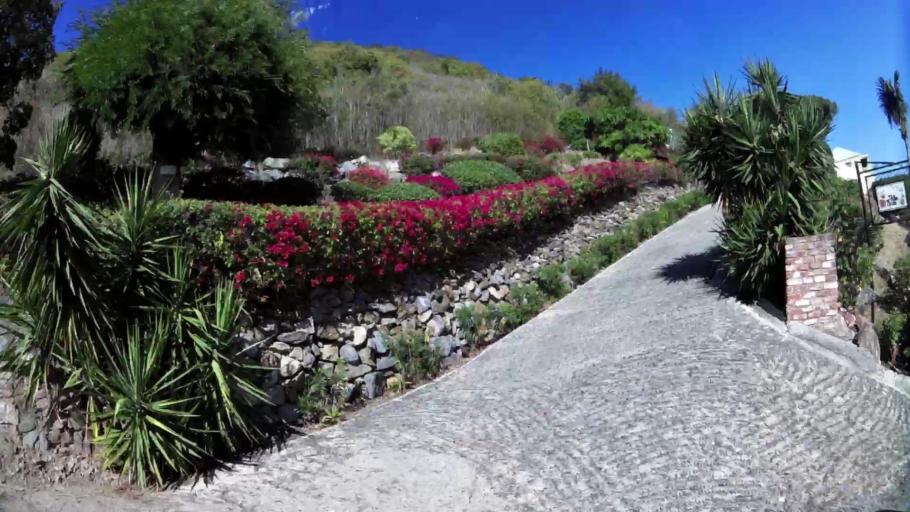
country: VG
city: Road Town
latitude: 18.3889
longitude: -64.6984
